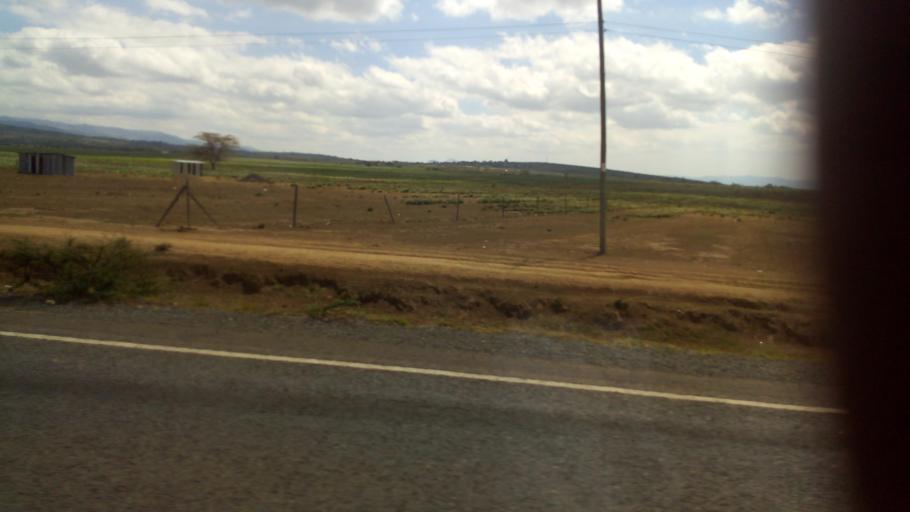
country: KE
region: Narok
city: Narok
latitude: -1.1062
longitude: 36.2318
